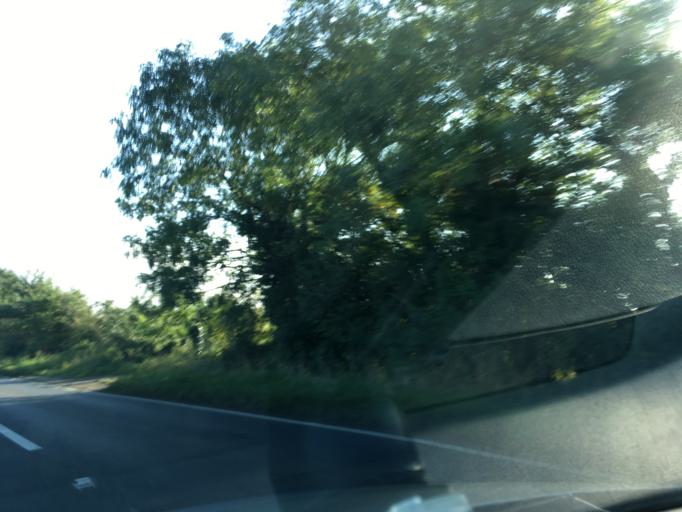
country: GB
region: England
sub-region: Oxfordshire
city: Claydon
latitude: 52.1123
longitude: -1.2874
